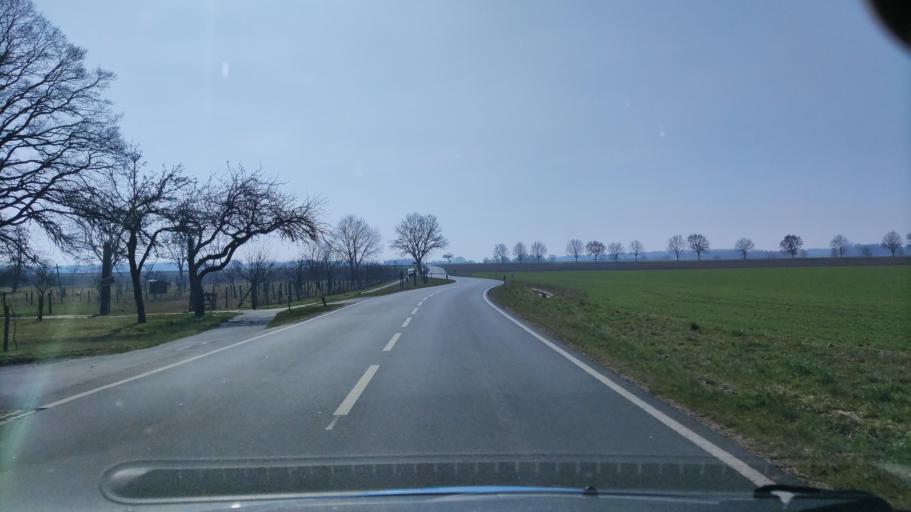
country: DE
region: Lower Saxony
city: Clenze
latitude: 52.9659
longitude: 10.9720
